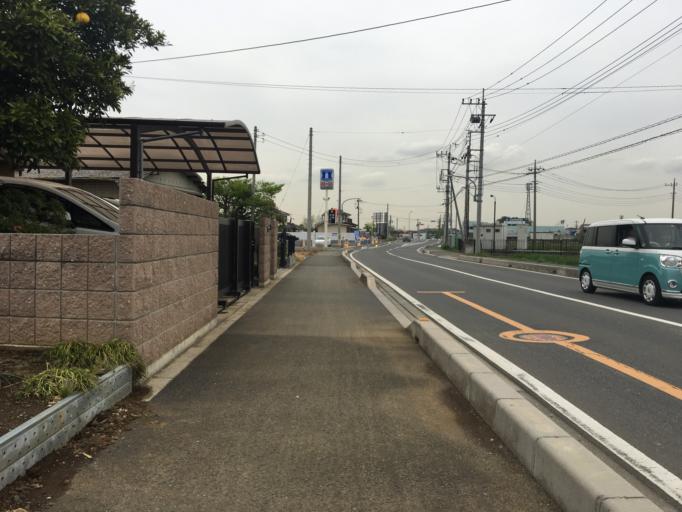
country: JP
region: Saitama
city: Oi
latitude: 35.8539
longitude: 139.5539
